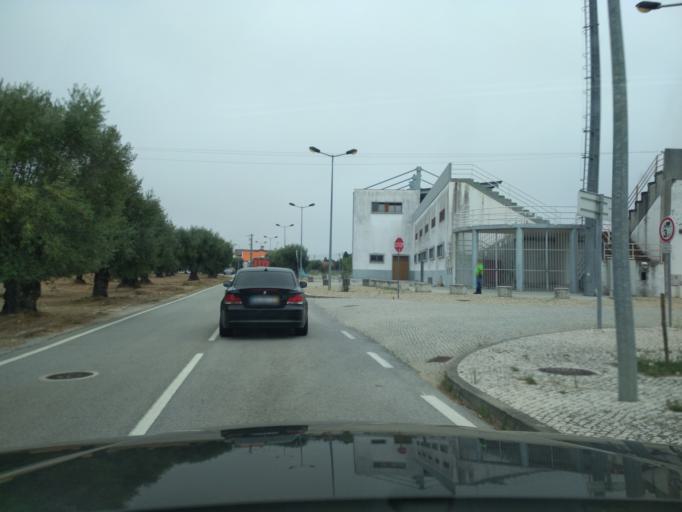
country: PT
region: Aveiro
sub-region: Mealhada
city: Mealhada
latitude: 40.3732
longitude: -8.4557
